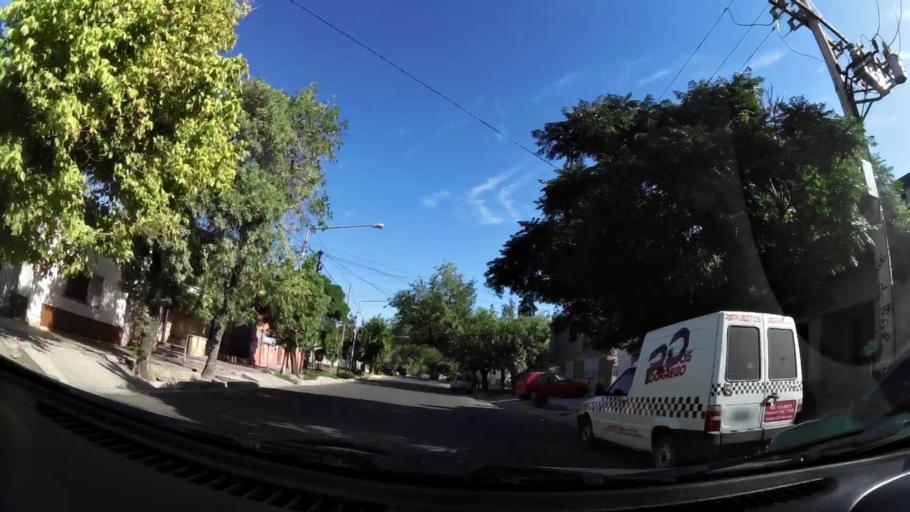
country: AR
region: Mendoza
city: Mendoza
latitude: -32.9054
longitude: -68.8330
